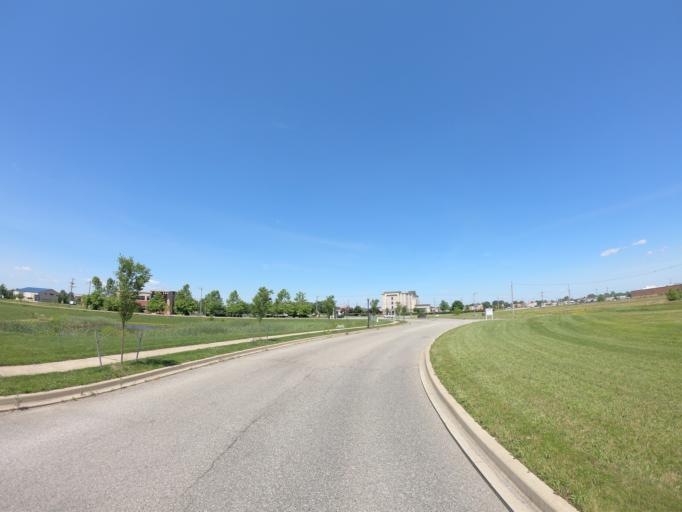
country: US
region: Delaware
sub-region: New Castle County
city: Middletown
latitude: 39.4504
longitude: -75.7326
